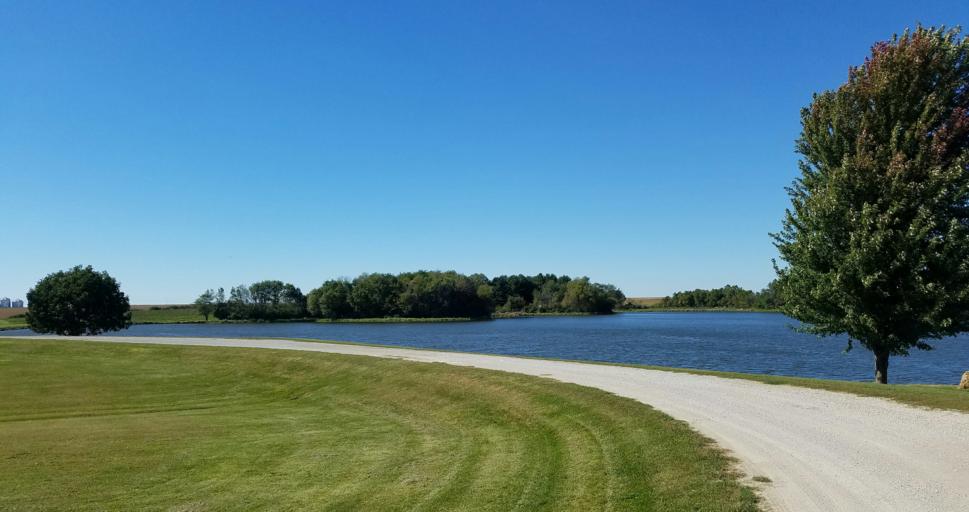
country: US
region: Iowa
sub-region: Decatur County
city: Lamoni
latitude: 40.6275
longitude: -93.9464
